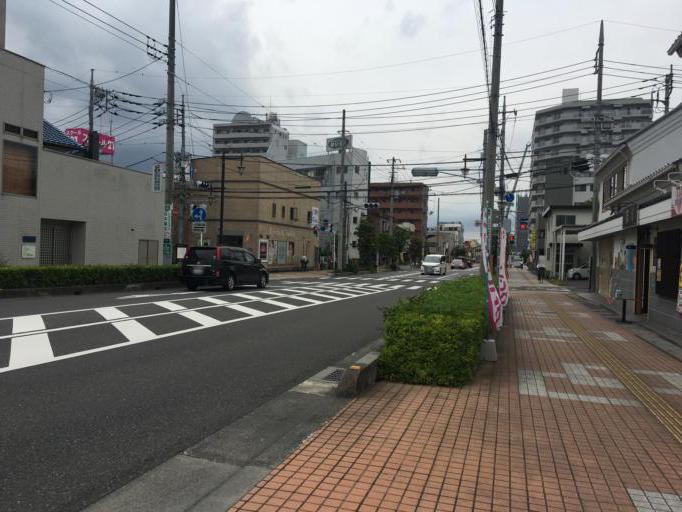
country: JP
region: Saitama
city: Kasukabe
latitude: 35.9811
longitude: 139.7549
